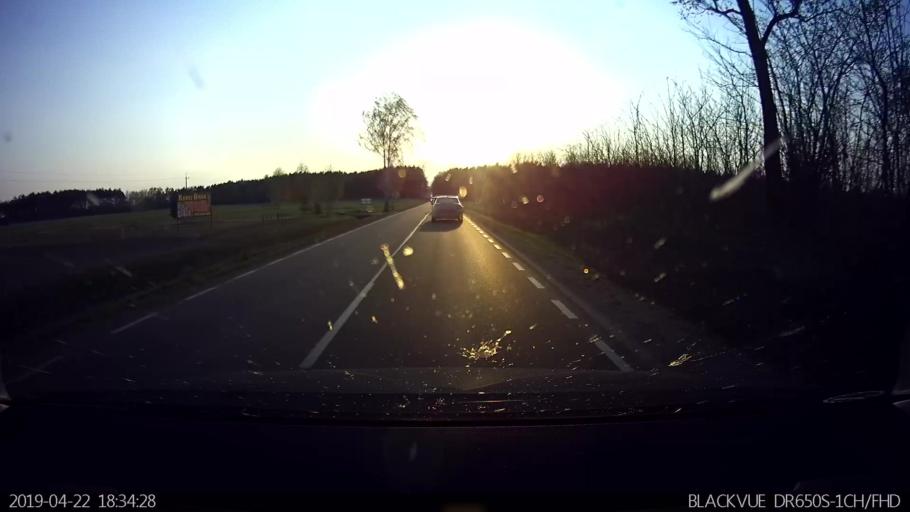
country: PL
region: Masovian Voivodeship
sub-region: Powiat wolominski
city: Jasienica
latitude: 52.4453
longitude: 21.3683
